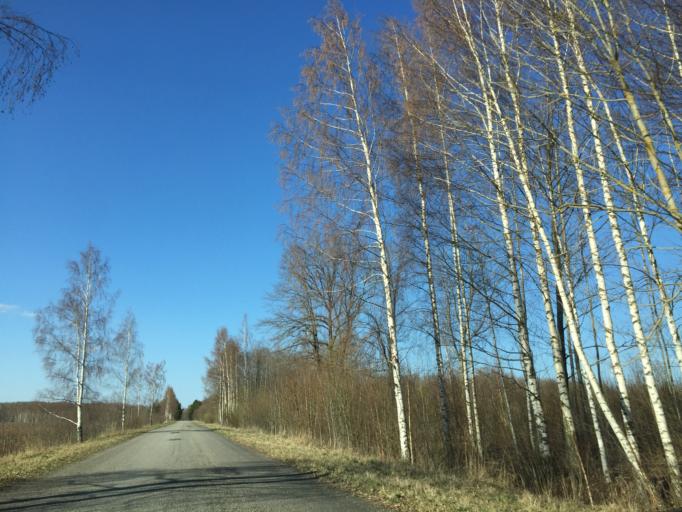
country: EE
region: Valgamaa
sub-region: Torva linn
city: Torva
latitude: 58.2462
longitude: 25.9489
